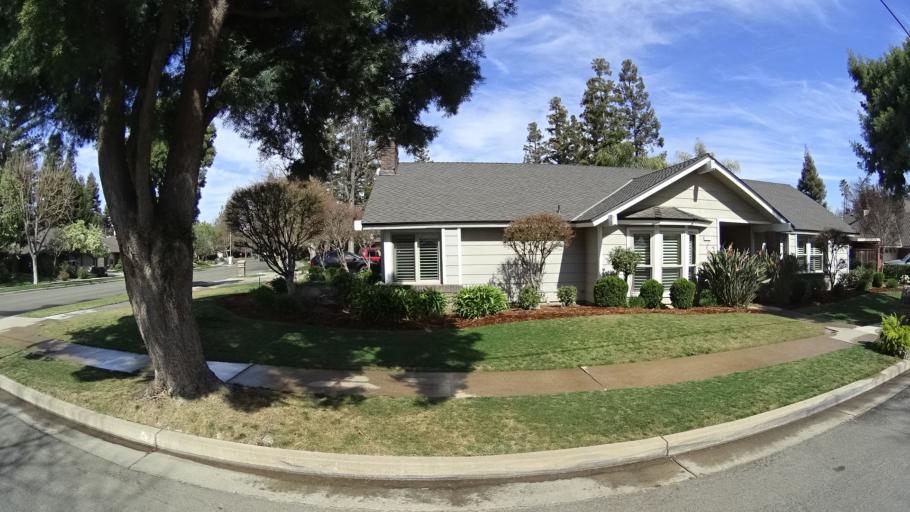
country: US
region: California
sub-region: Fresno County
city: Clovis
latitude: 36.8592
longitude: -119.7735
